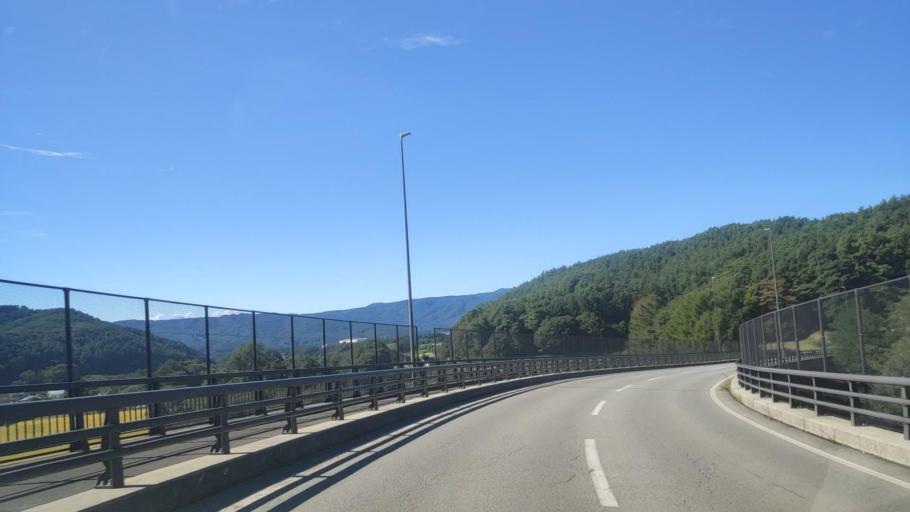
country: JP
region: Nagano
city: Chino
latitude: 35.9940
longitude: 138.2139
